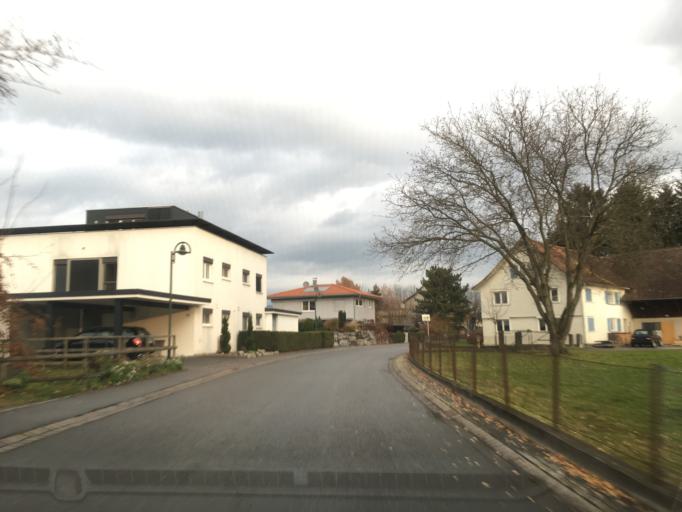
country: AT
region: Vorarlberg
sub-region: Politischer Bezirk Feldkirch
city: Mader
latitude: 47.3450
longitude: 9.6224
